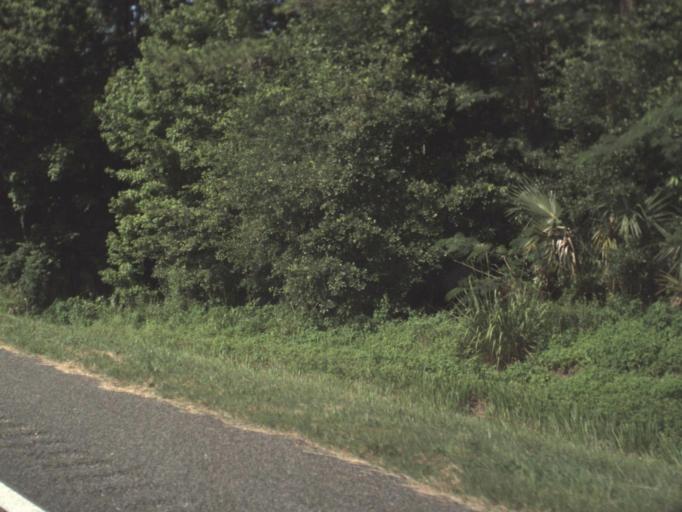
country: US
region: Florida
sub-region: Alachua County
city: Gainesville
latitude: 29.5305
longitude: -82.3089
